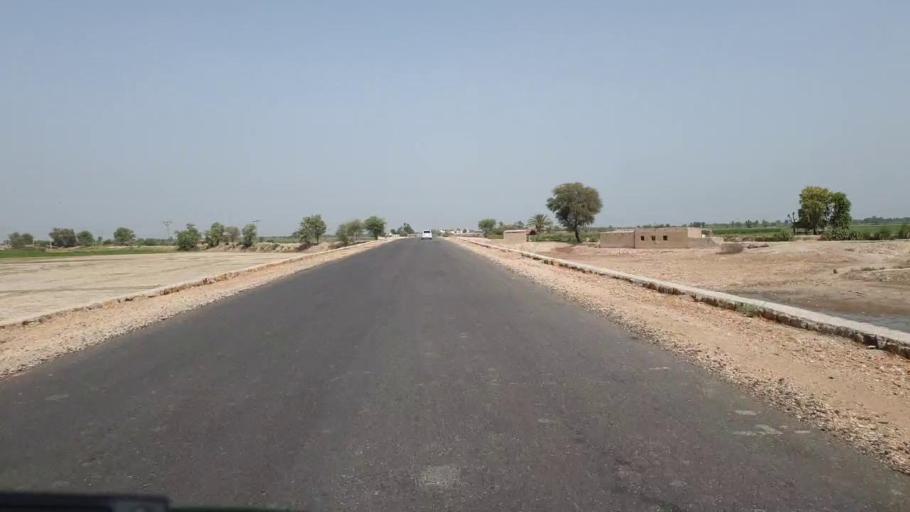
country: PK
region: Sindh
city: Sakrand
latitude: 26.2667
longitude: 68.1708
